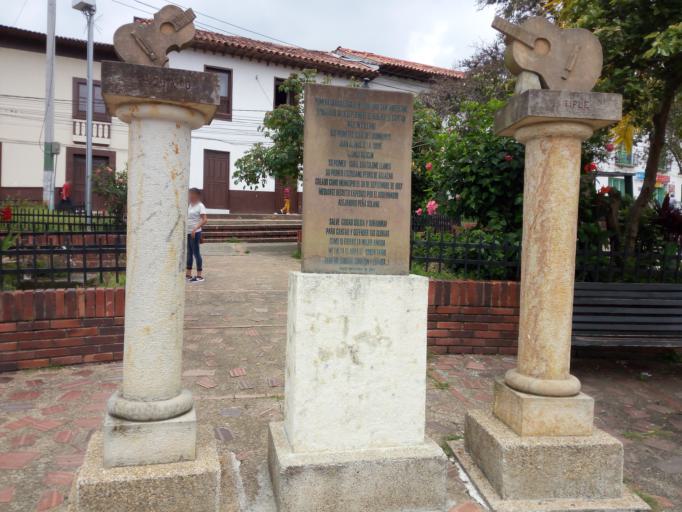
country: CO
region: Santander
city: Velez
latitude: 6.0127
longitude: -73.6720
